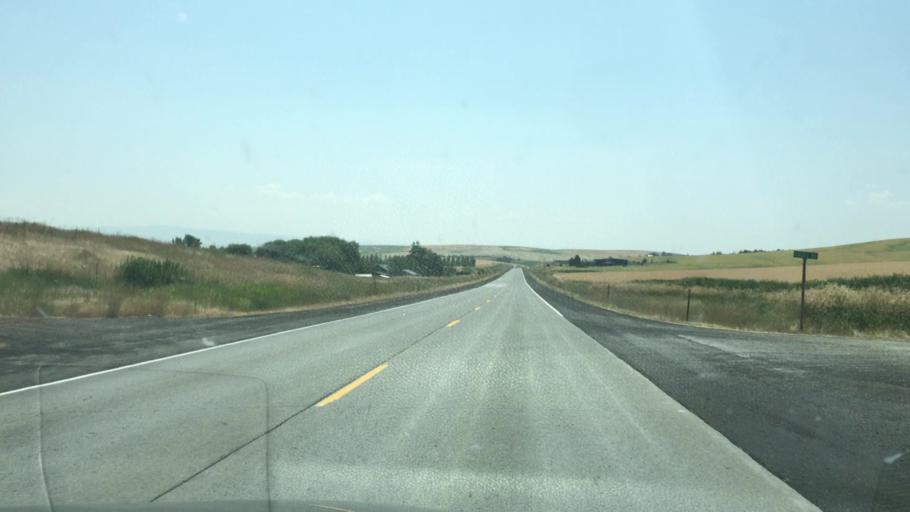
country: US
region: Idaho
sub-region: Lewis County
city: Nezperce
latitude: 46.0851
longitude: -116.3458
